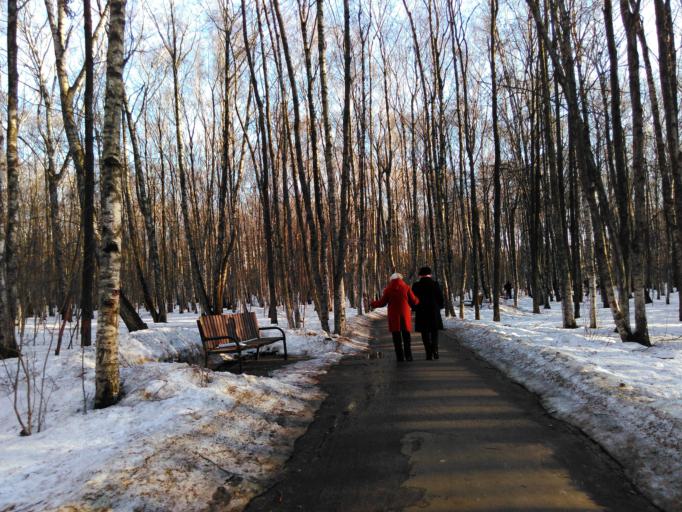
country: RU
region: Moscow
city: Troparevo
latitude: 55.6558
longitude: 37.5046
